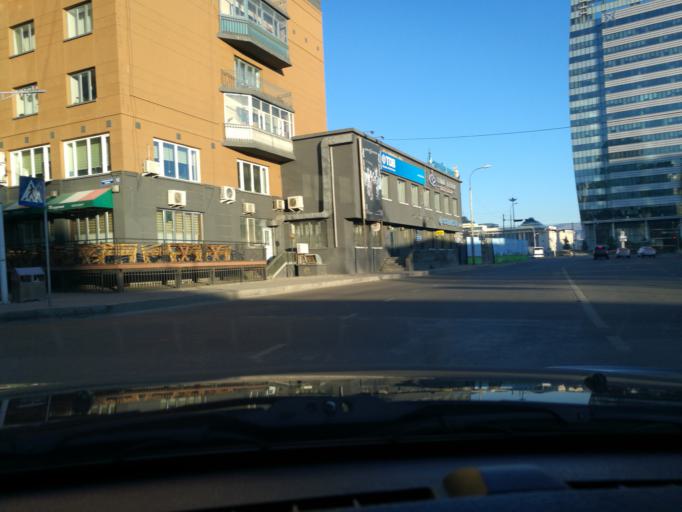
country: MN
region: Ulaanbaatar
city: Ulaanbaatar
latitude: 47.9162
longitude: 106.9203
